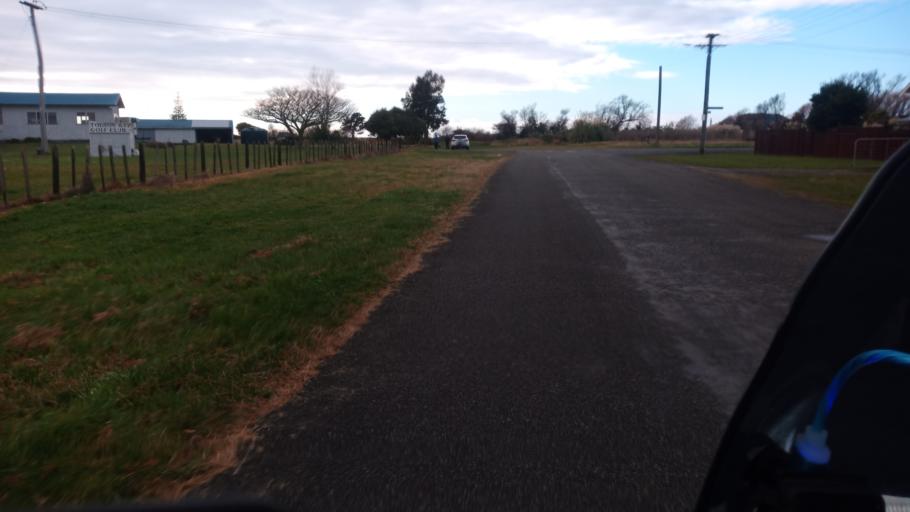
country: NZ
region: Gisborne
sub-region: Gisborne District
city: Gisborne
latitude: -38.3696
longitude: 178.3021
